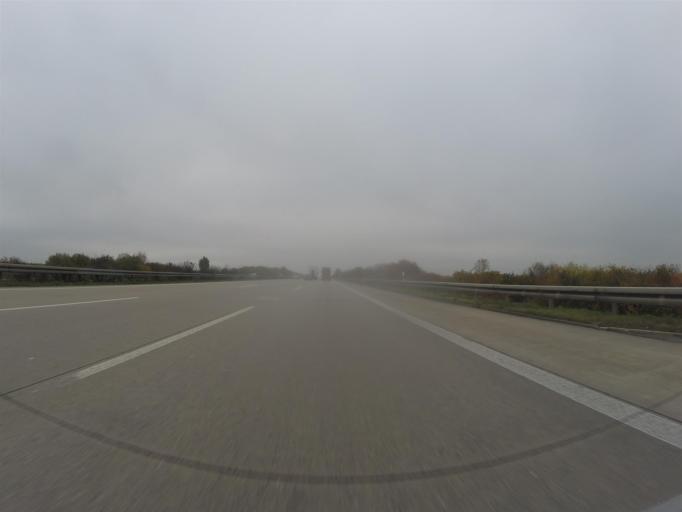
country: DE
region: Thuringia
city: Walpernhain
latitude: 51.0131
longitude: 11.9268
